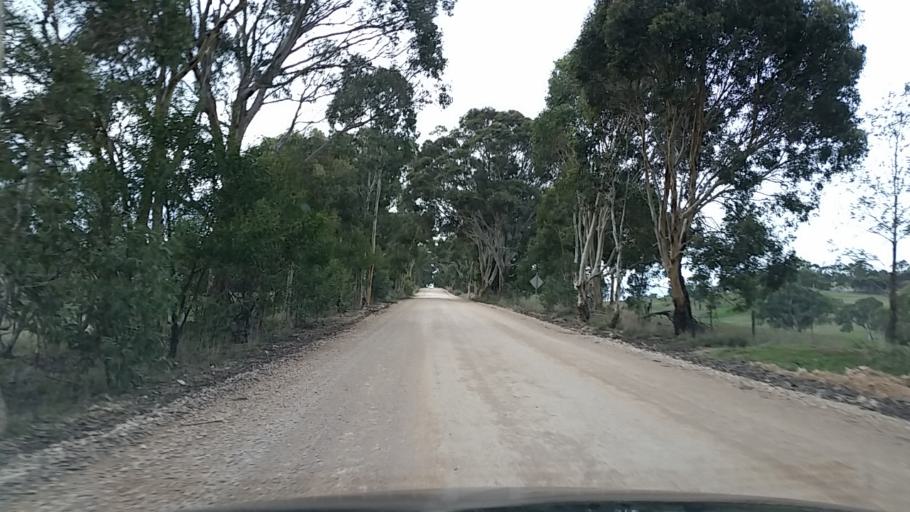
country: AU
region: South Australia
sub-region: Adelaide Hills
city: Birdwood
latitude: -34.9140
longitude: 139.0215
